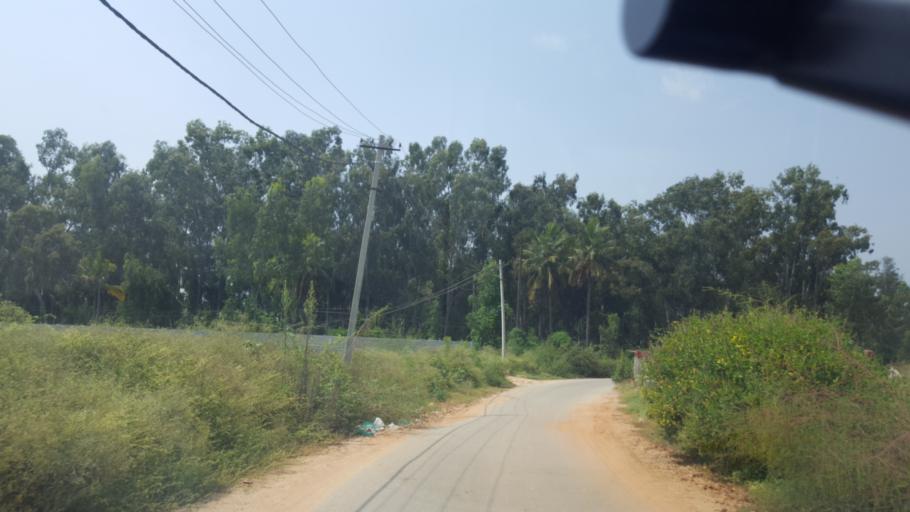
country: IN
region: Karnataka
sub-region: Bangalore Urban
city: Bangalore
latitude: 12.9375
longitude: 77.7085
